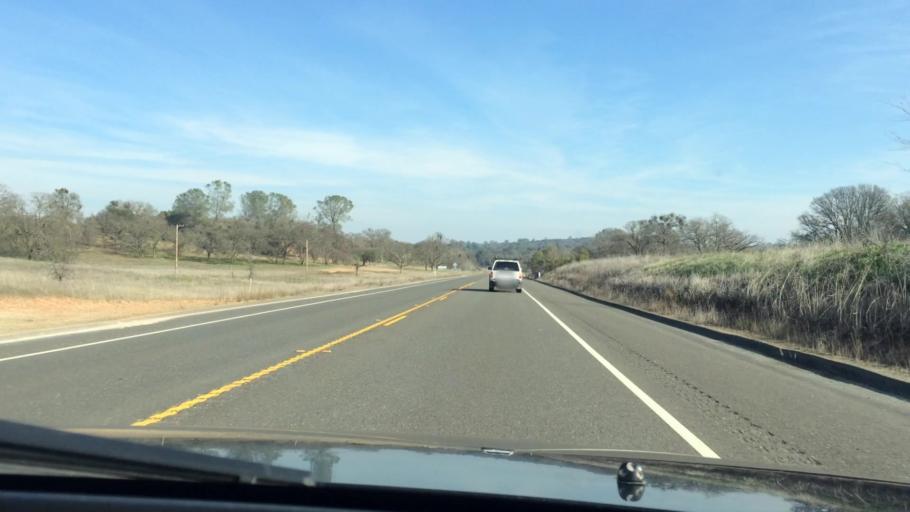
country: US
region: California
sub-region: Sacramento County
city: Rancho Murieta
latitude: 38.4808
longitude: -121.0331
